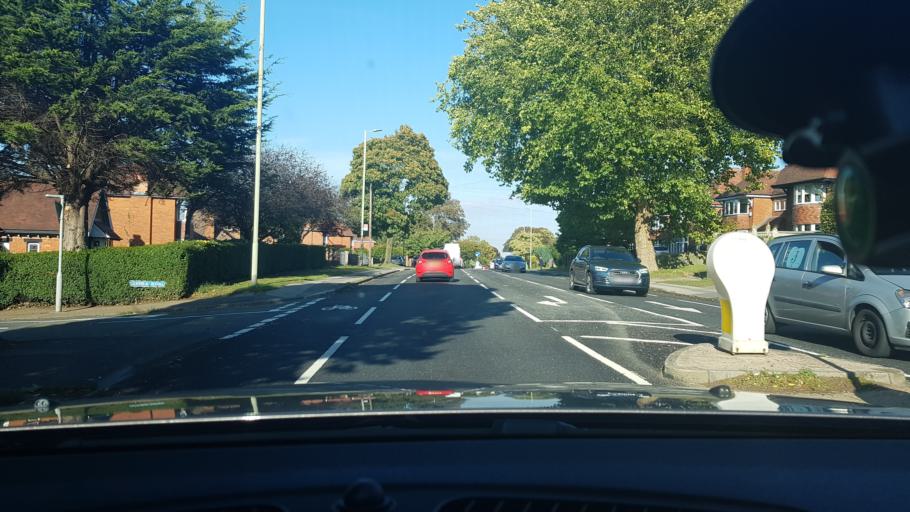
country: GB
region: England
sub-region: Gloucestershire
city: Gloucester
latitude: 51.8417
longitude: -2.2405
